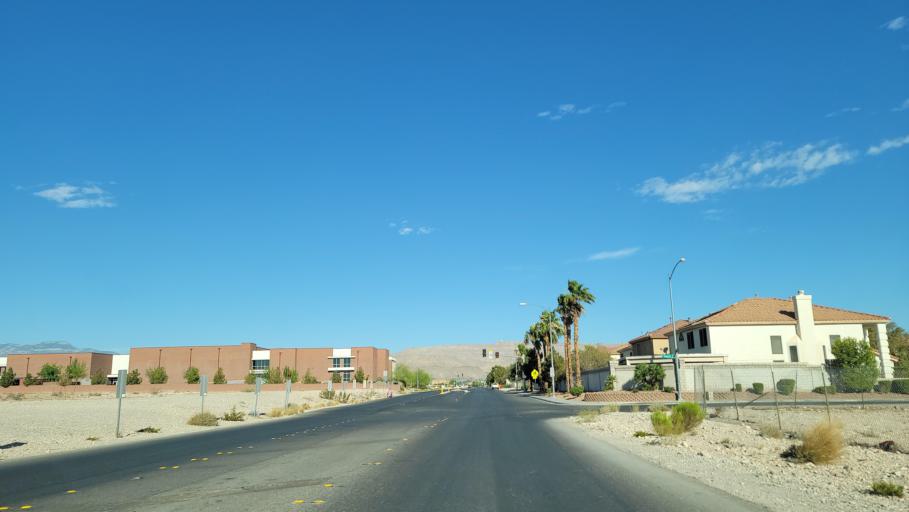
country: US
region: Nevada
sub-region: Clark County
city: Spring Valley
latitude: 36.0777
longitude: -115.2719
